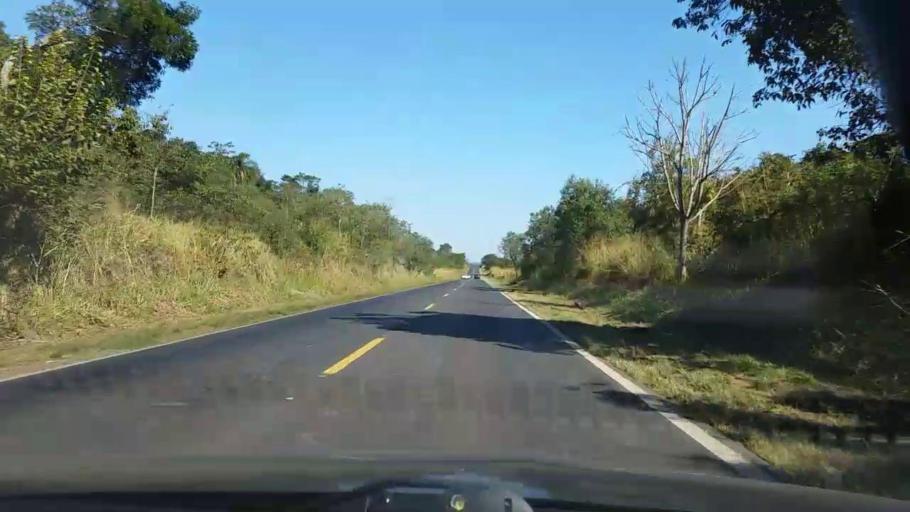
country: BR
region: Sao Paulo
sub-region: Itatinga
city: Itatinga
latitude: -22.8966
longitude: -48.7641
